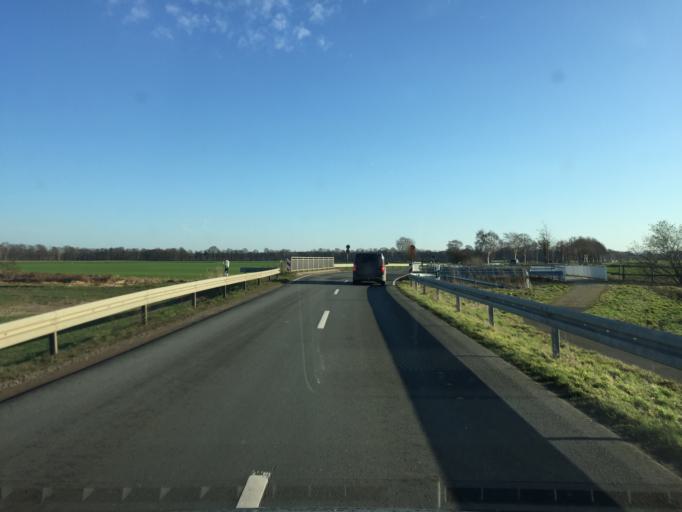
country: DE
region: Lower Saxony
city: Estorf
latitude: 52.5571
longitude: 9.1776
